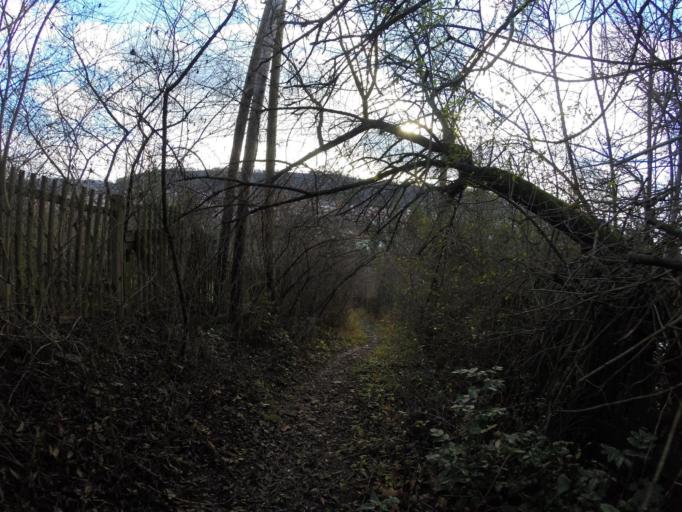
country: DE
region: Thuringia
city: Jena
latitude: 50.9353
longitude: 11.6233
